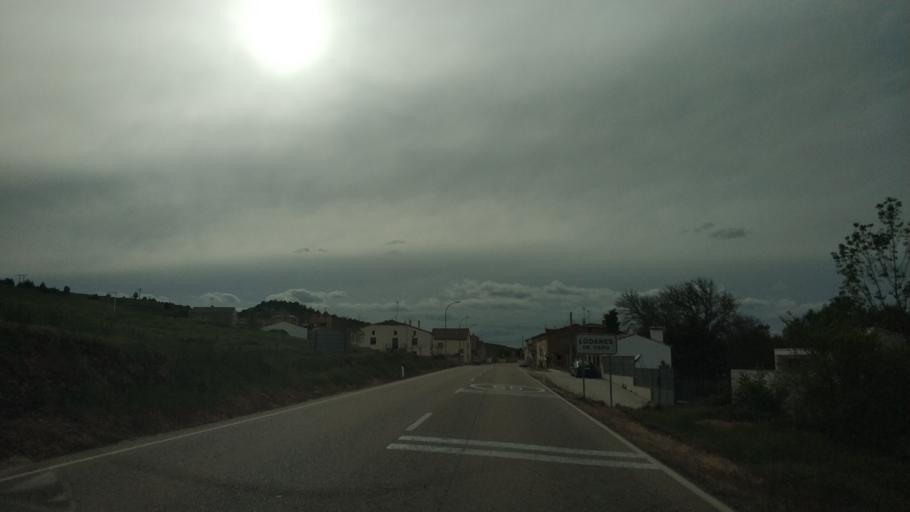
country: ES
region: Castille and Leon
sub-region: Provincia de Soria
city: Valdenebro
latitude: 41.5692
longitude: -3.0075
